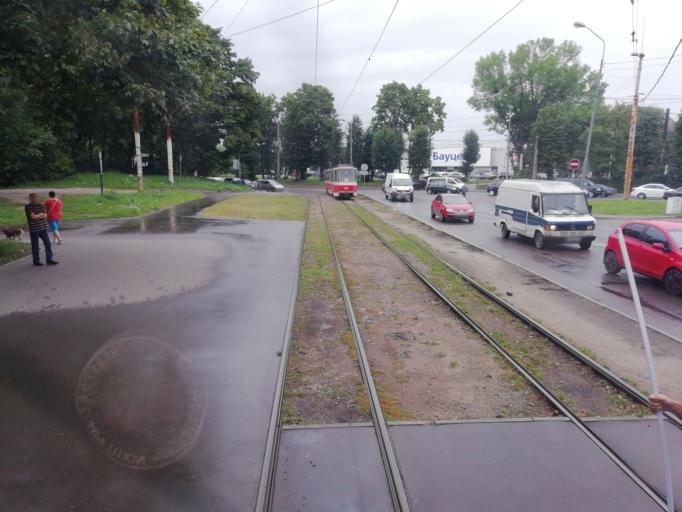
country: RU
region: Kaliningrad
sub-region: Gorod Kaliningrad
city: Kaliningrad
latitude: 54.6939
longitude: 20.5240
